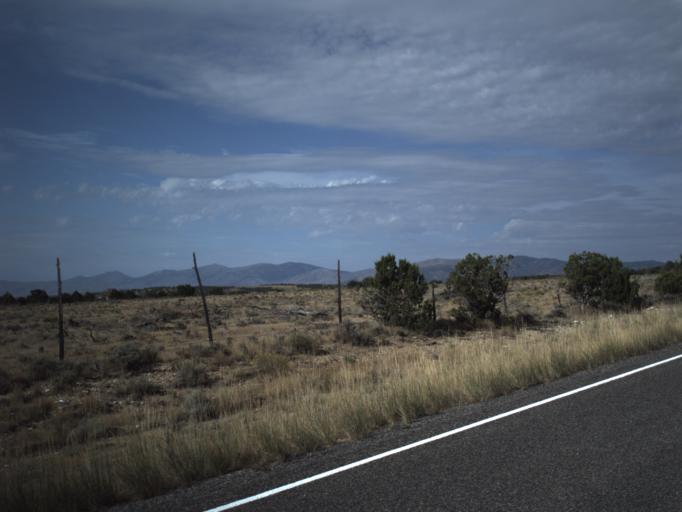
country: US
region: Idaho
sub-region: Cassia County
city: Burley
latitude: 41.8177
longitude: -113.3950
